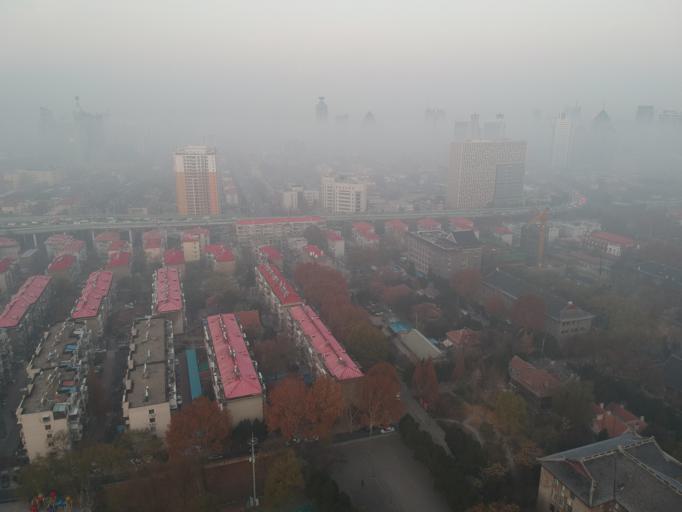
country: CN
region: Shandong Sheng
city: Jinan
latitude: 36.6511
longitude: 117.0125
